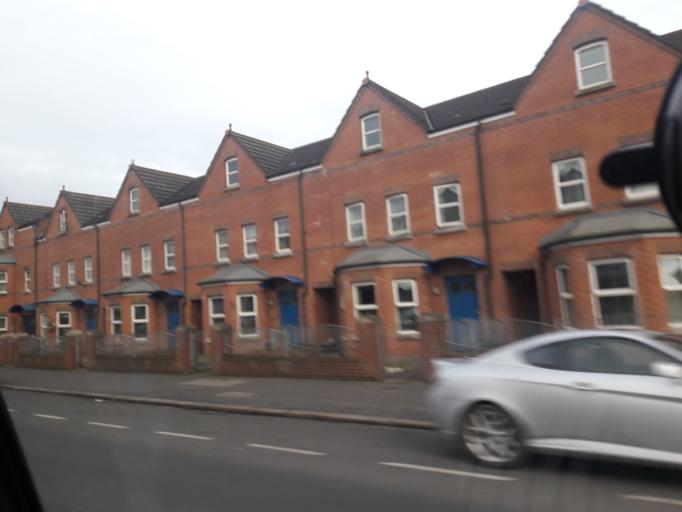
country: GB
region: Northern Ireland
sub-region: City of Belfast
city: Belfast
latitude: 54.6173
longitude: -5.9239
